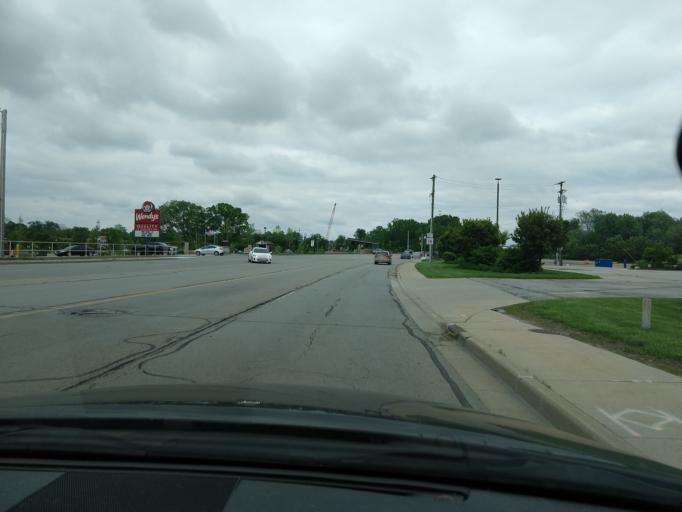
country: US
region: Indiana
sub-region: Hamilton County
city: Noblesville
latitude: 40.0469
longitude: -86.0216
